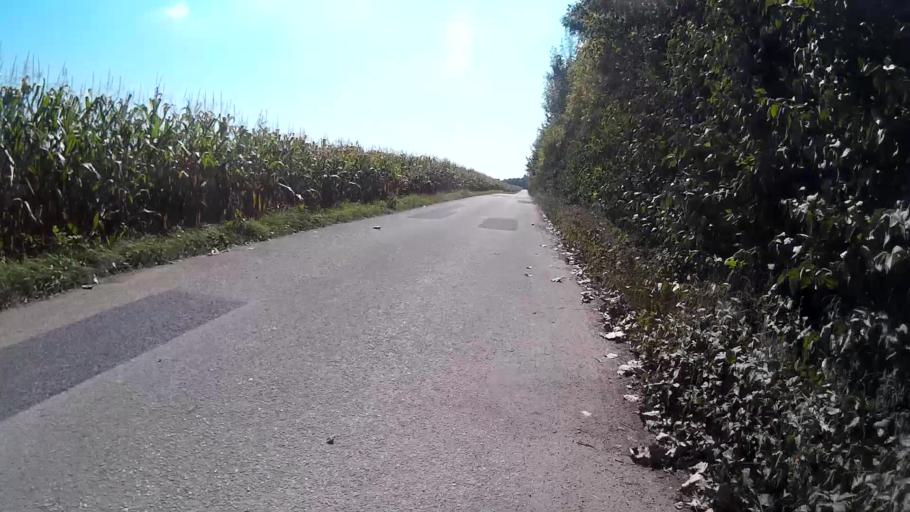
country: AT
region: Lower Austria
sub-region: Politischer Bezirk Mistelbach
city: Neudorf bei Staatz
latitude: 48.7667
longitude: 16.4884
